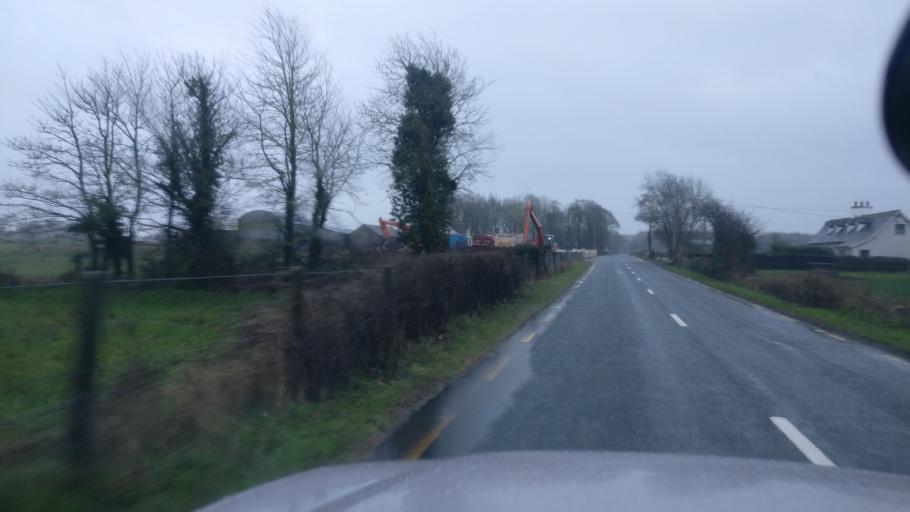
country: IE
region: Connaught
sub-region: County Galway
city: Ballinasloe
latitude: 53.2645
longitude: -8.1911
